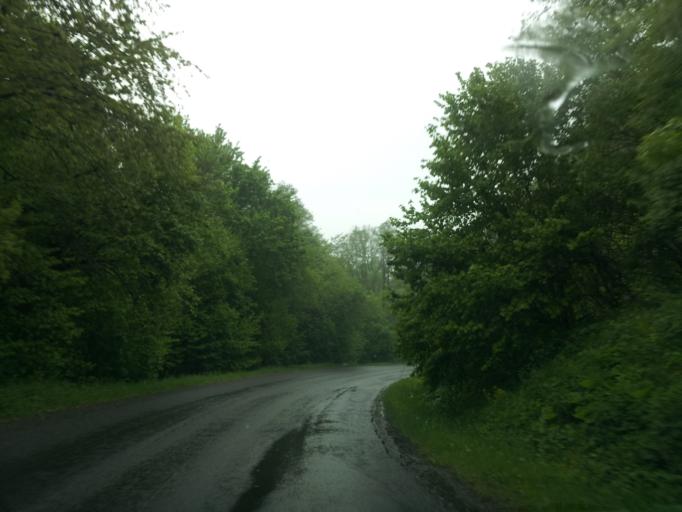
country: HU
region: Baranya
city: Komlo
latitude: 46.2212
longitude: 18.3023
